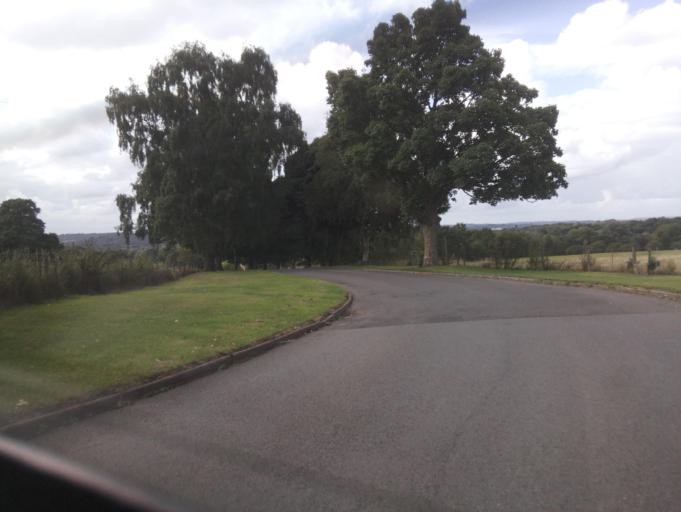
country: GB
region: England
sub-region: Staffordshire
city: Barlaston
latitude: 52.9508
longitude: -2.1583
